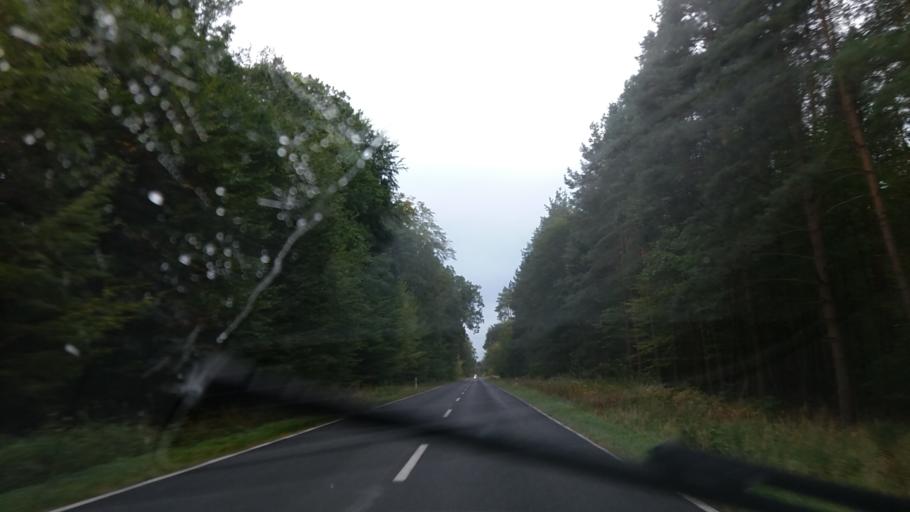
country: PL
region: West Pomeranian Voivodeship
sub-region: Powiat mysliborski
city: Barlinek
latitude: 52.9204
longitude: 15.1940
